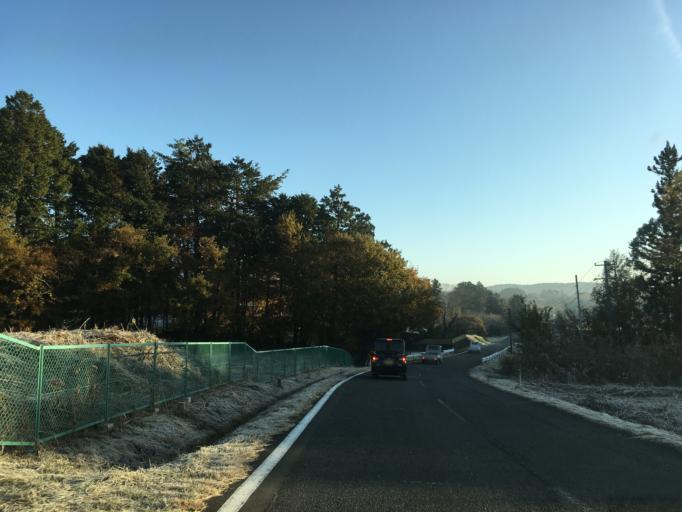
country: JP
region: Iwate
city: Ichinoseki
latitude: 38.7982
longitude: 141.1959
